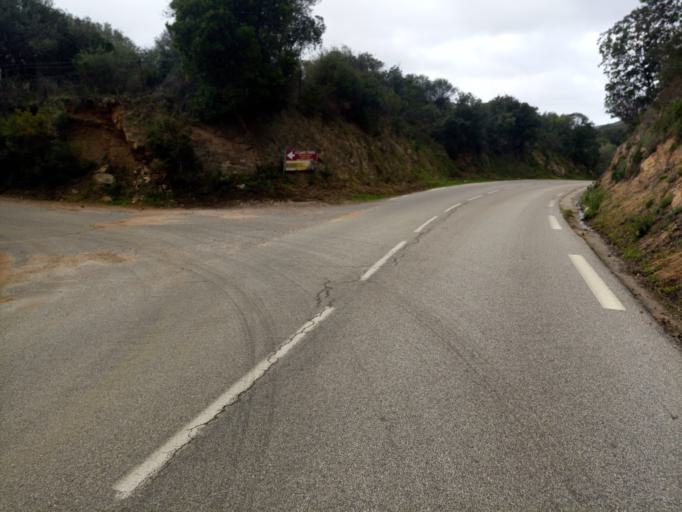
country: FR
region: Corsica
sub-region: Departement de la Corse-du-Sud
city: Sartene
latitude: 41.5491
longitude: 8.8904
